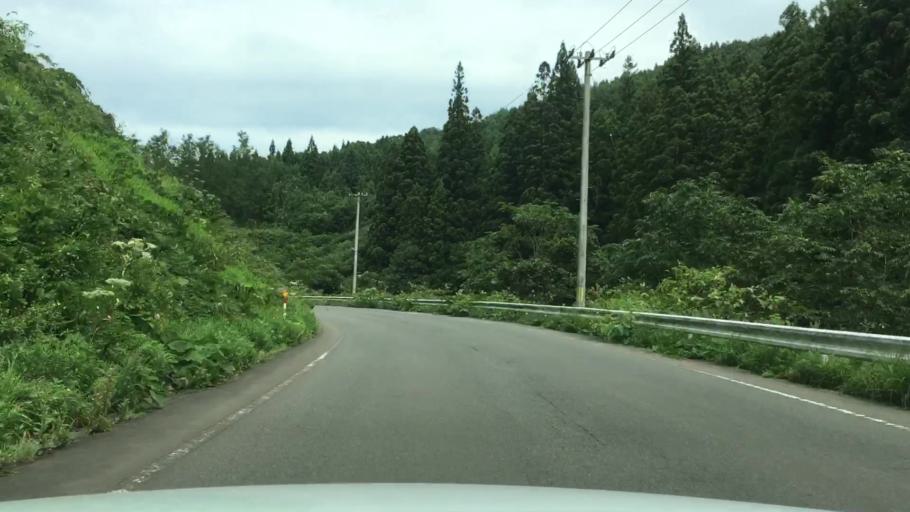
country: JP
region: Aomori
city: Shimokizukuri
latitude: 40.7409
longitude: 140.2448
